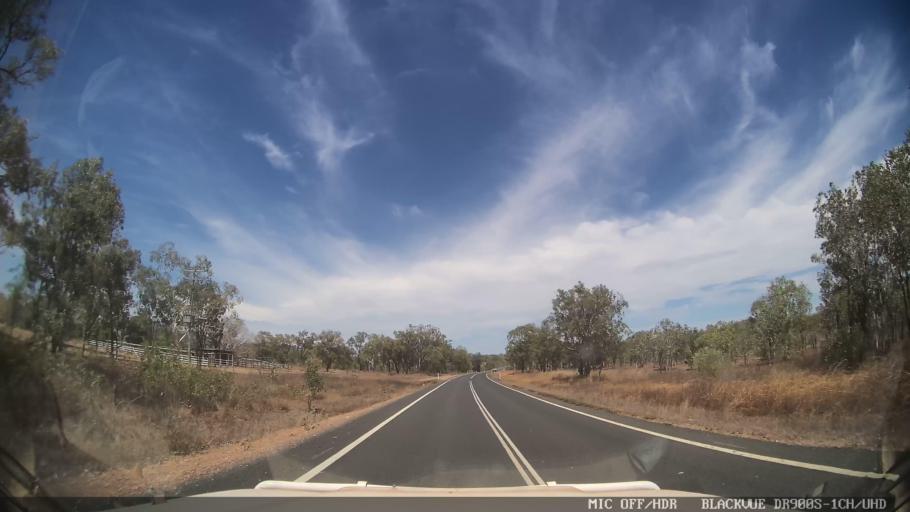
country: AU
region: Queensland
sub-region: Cook
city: Cooktown
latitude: -15.8736
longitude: 144.8607
